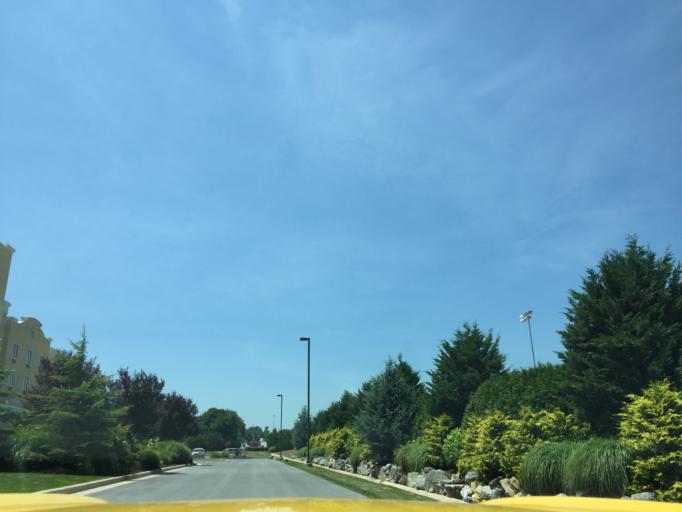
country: US
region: West Virginia
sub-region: Jefferson County
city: Ranson
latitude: 39.2956
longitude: -77.8465
